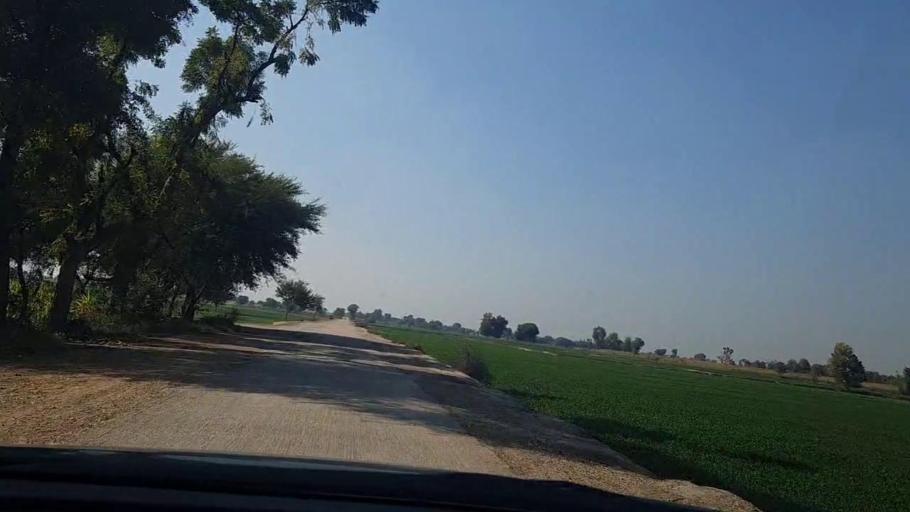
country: PK
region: Sindh
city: Daulatpur
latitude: 26.2847
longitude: 68.0674
